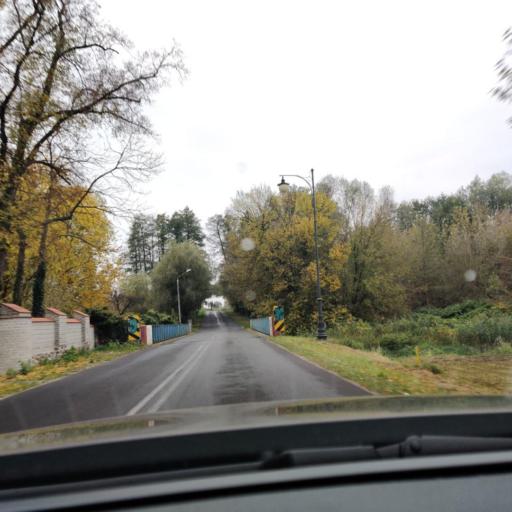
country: PL
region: Masovian Voivodeship
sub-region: Powiat sochaczewski
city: Sochaczew
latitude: 52.2567
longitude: 20.3091
